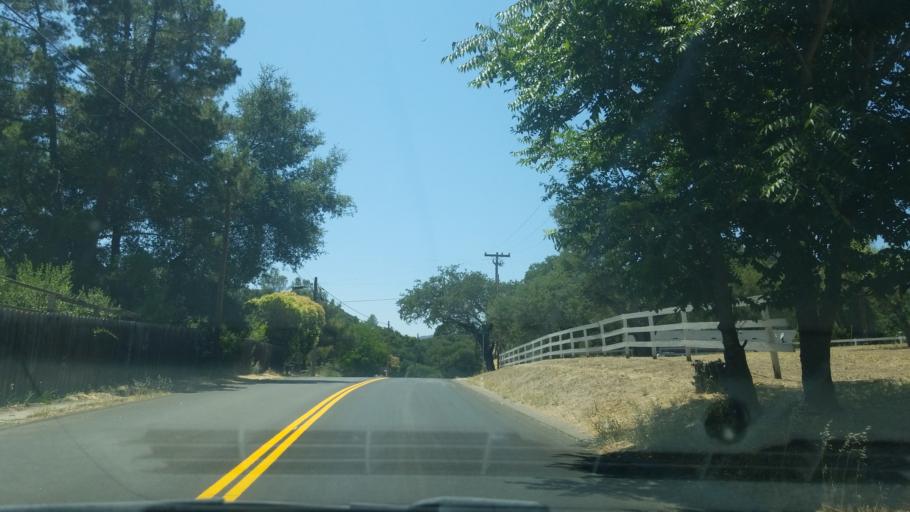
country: US
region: California
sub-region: San Luis Obispo County
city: Atascadero
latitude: 35.4850
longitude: -120.6500
